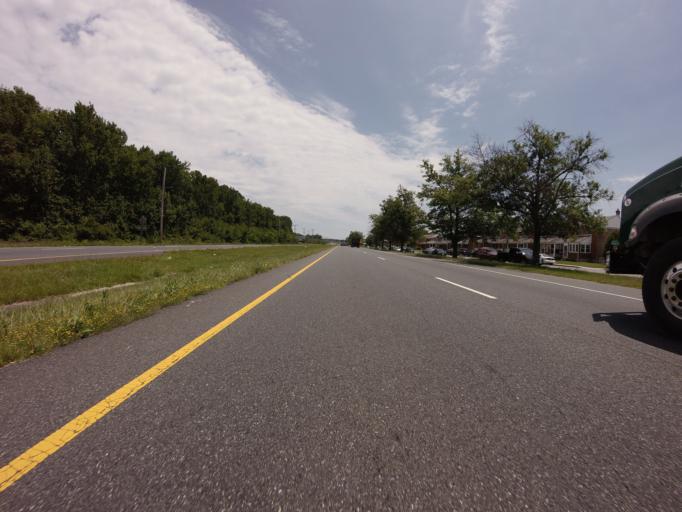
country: US
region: Maryland
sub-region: Baltimore County
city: Essex
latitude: 39.2798
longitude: -76.4838
